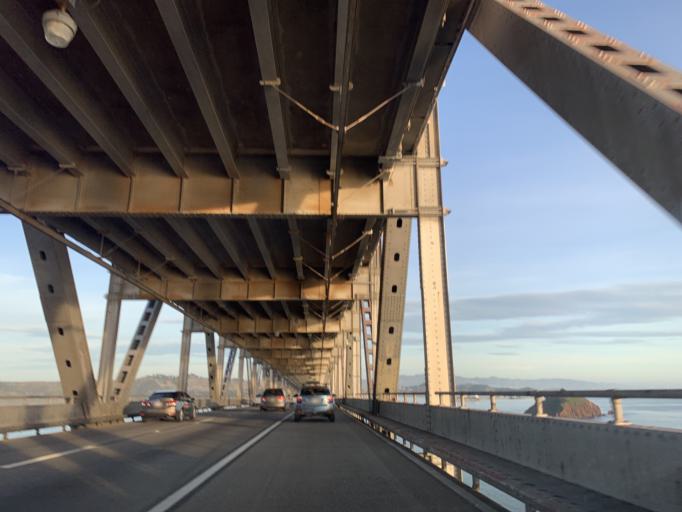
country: US
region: California
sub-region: Marin County
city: Tiburon
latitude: 37.9350
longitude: -122.4442
